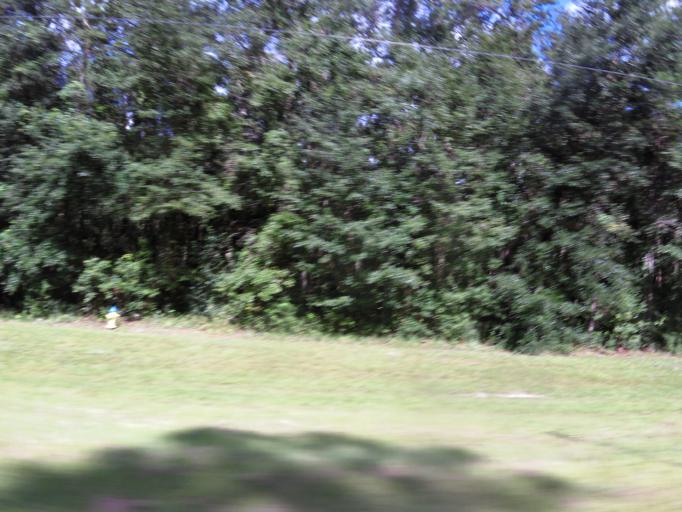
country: US
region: Georgia
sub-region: Camden County
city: Kingsland
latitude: 30.7854
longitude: -81.6872
